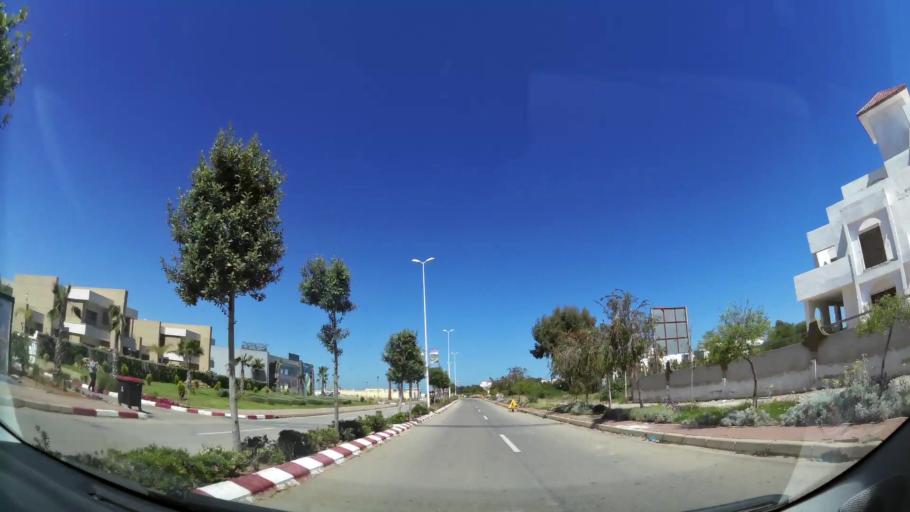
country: MA
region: Oriental
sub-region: Berkane-Taourirt
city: Madagh
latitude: 35.1092
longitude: -2.3135
